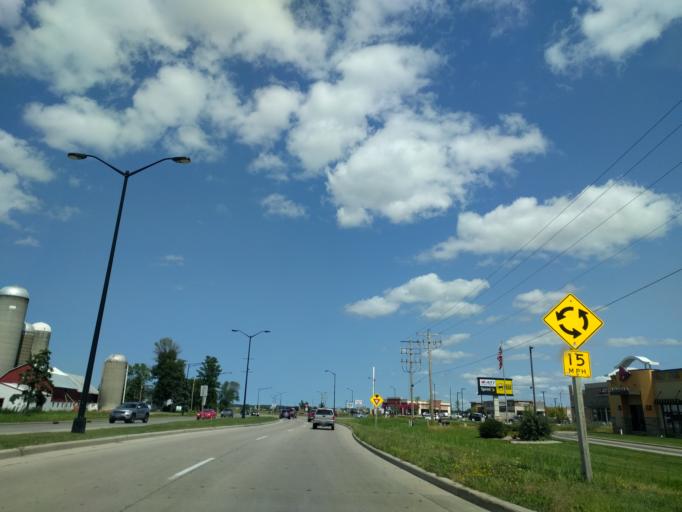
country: US
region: Wisconsin
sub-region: Brown County
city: Allouez
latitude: 44.4575
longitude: -87.9908
